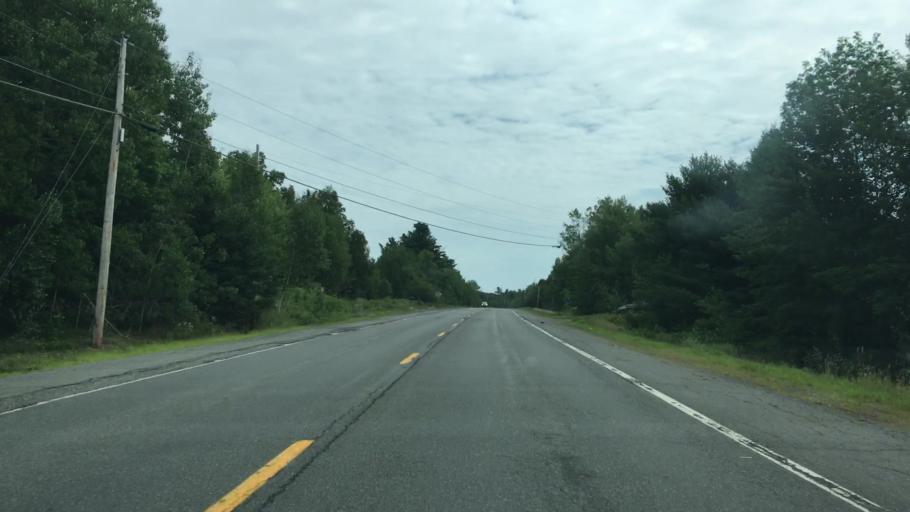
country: US
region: Maine
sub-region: Washington County
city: Calais
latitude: 45.1124
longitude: -67.4201
